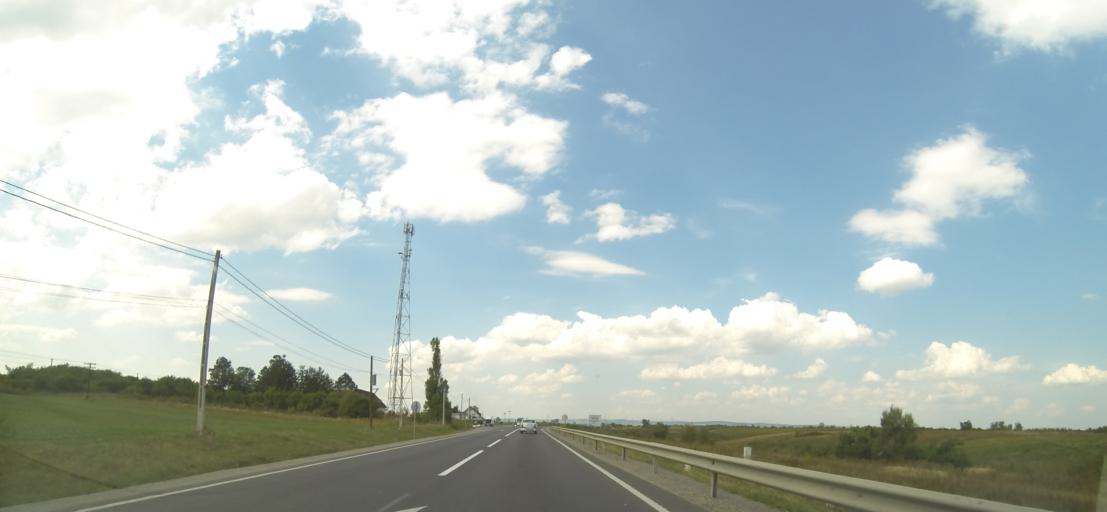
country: RO
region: Brasov
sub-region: Comuna Sinca Veche
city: Persani
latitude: 45.7882
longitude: 25.1982
